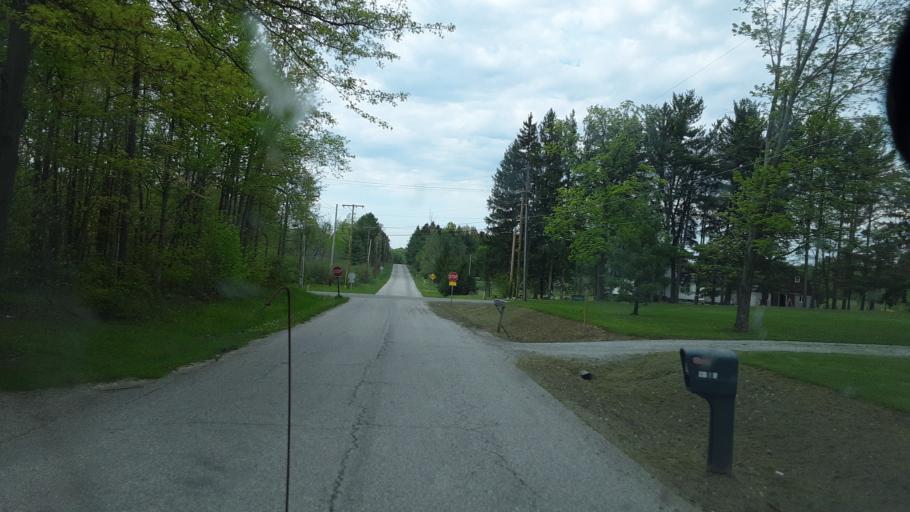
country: US
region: Ohio
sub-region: Portage County
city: Garrettsville
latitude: 41.3472
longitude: -81.0222
